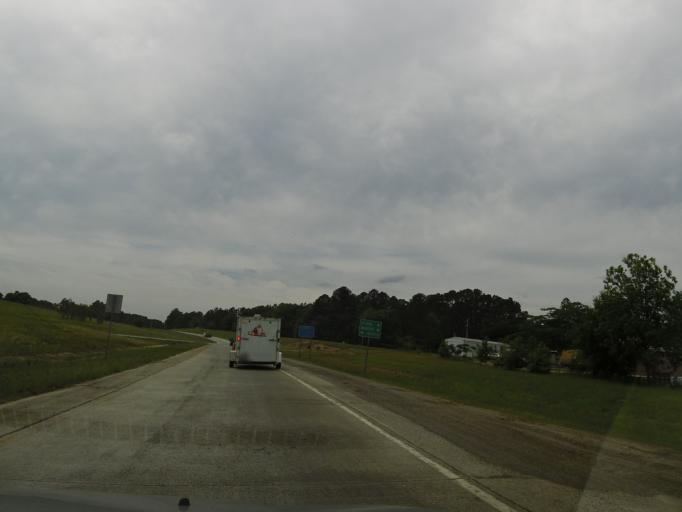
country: US
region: Georgia
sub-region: Candler County
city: Metter
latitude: 32.3753
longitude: -82.1649
